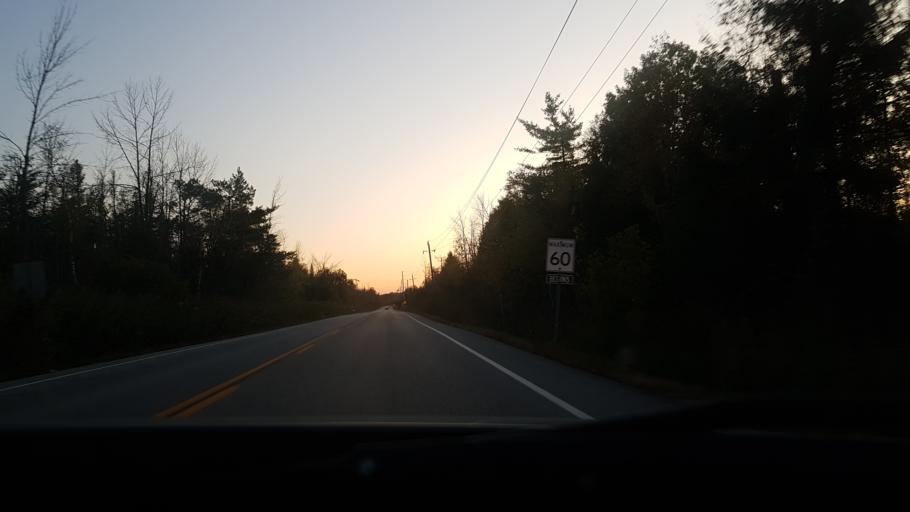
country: CA
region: Ontario
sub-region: Halton
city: Milton
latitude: 43.4778
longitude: -79.9904
